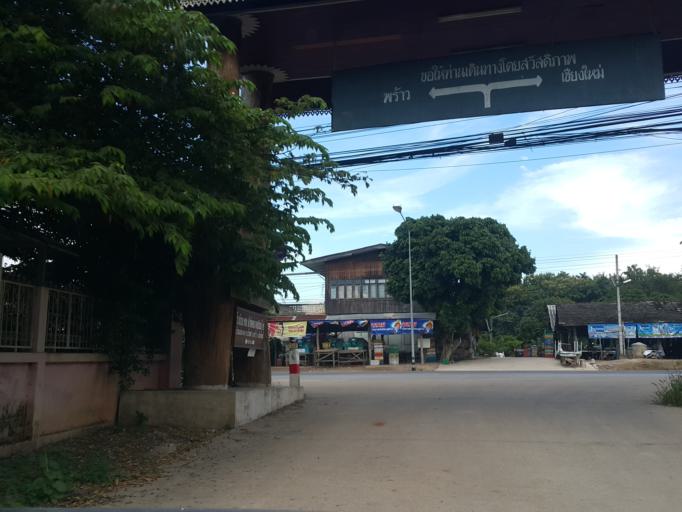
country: TH
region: Chiang Mai
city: Phrao
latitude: 19.3356
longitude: 99.1933
